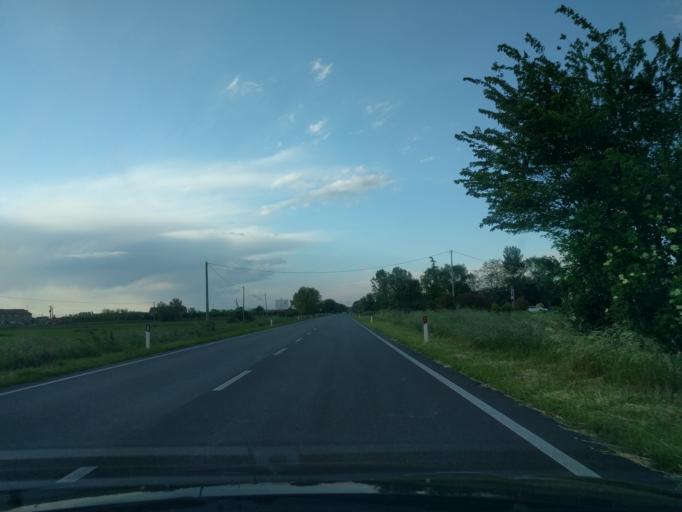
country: IT
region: Veneto
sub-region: Provincia di Rovigo
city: Polesella
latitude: 44.9462
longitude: 11.7351
